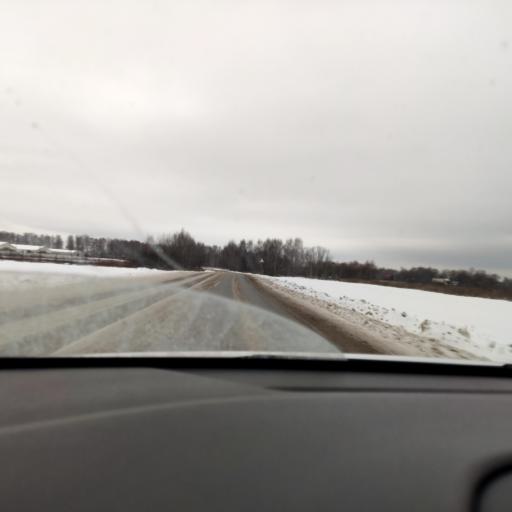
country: RU
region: Tatarstan
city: Osinovo
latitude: 55.8981
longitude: 48.8945
